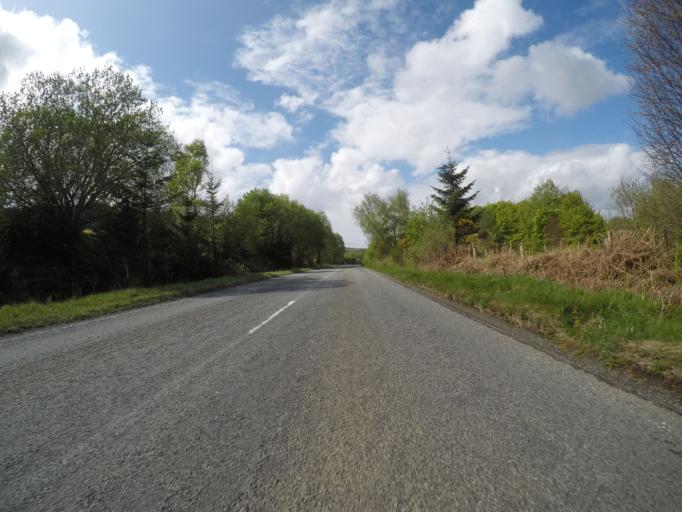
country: GB
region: Scotland
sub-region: Highland
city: Isle of Skye
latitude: 57.4529
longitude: -6.3123
